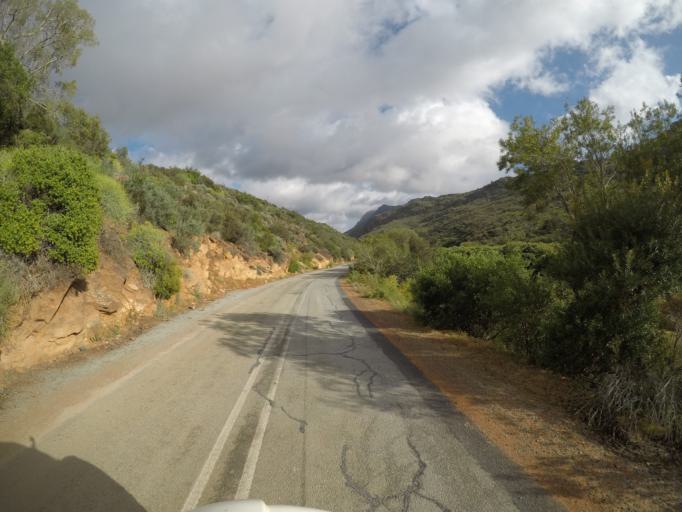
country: ZA
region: Western Cape
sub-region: West Coast District Municipality
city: Clanwilliam
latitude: -32.4170
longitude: 18.9260
